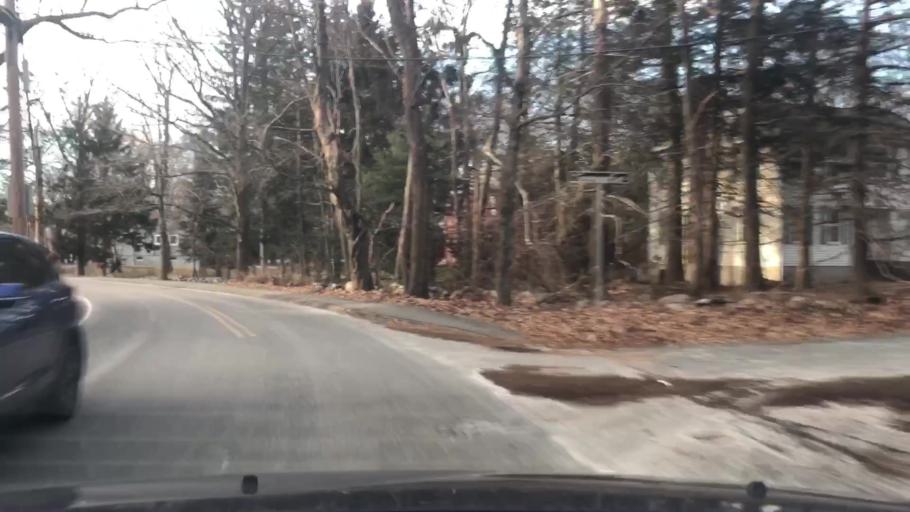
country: US
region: Massachusetts
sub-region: Essex County
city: Andover
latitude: 42.6717
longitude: -71.1114
